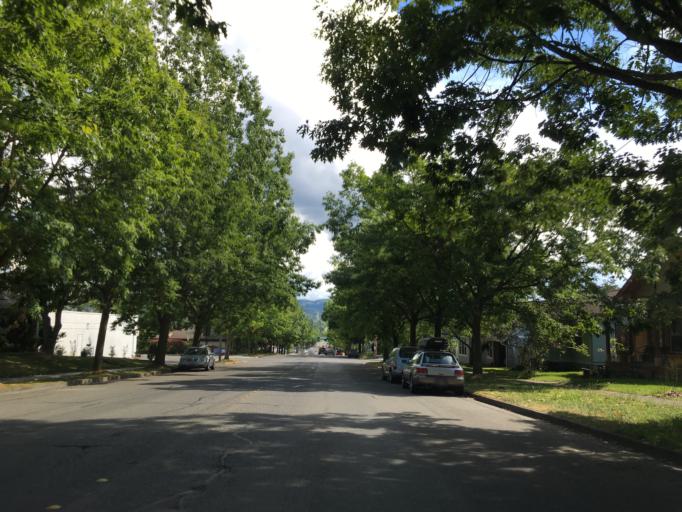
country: US
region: Washington
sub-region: Whatcom County
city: Bellingham
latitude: 48.7651
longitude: -122.4650
